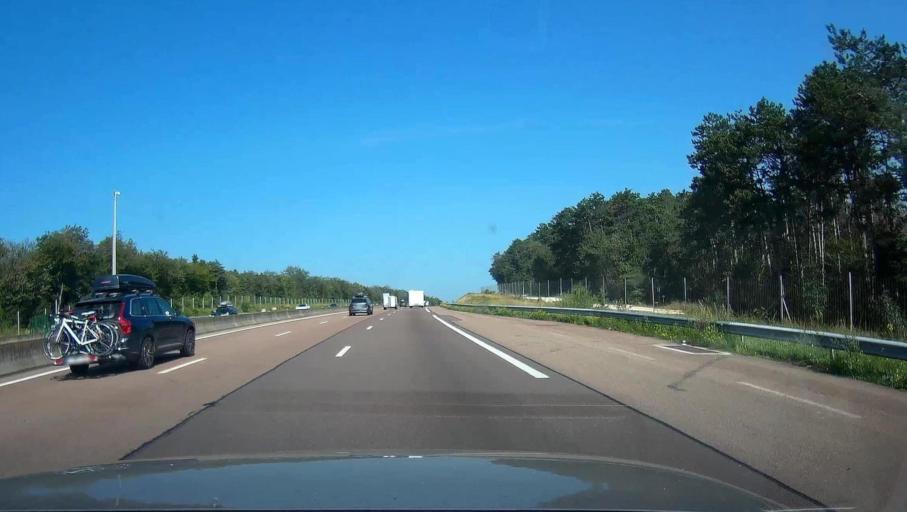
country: FR
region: Bourgogne
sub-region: Departement de la Cote-d'Or
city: Selongey
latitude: 47.6137
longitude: 5.1838
